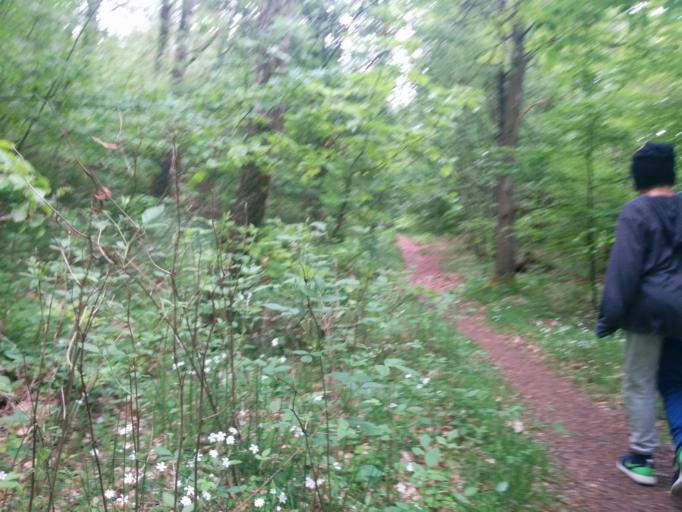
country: SE
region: Skane
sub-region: Lunds Kommun
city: Genarp
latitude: 55.5898
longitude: 13.3877
